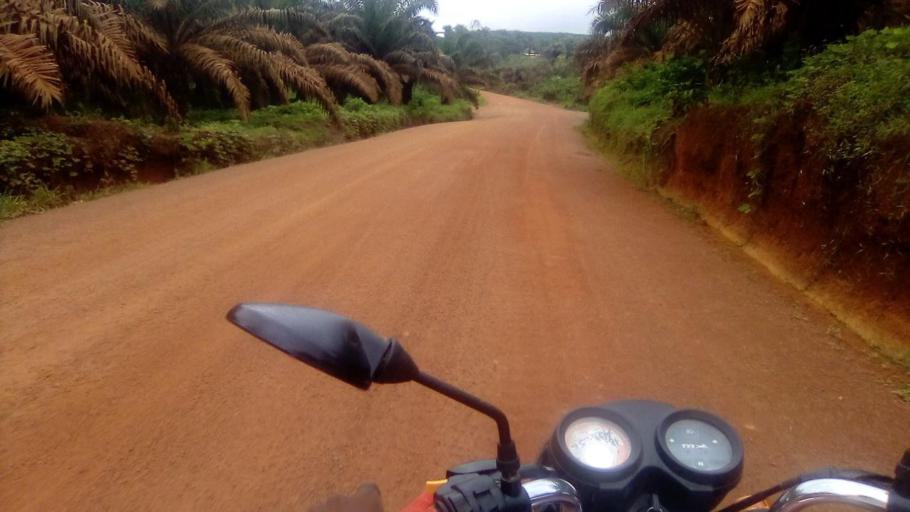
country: SL
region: Southern Province
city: Tongole
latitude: 7.4367
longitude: -11.8616
